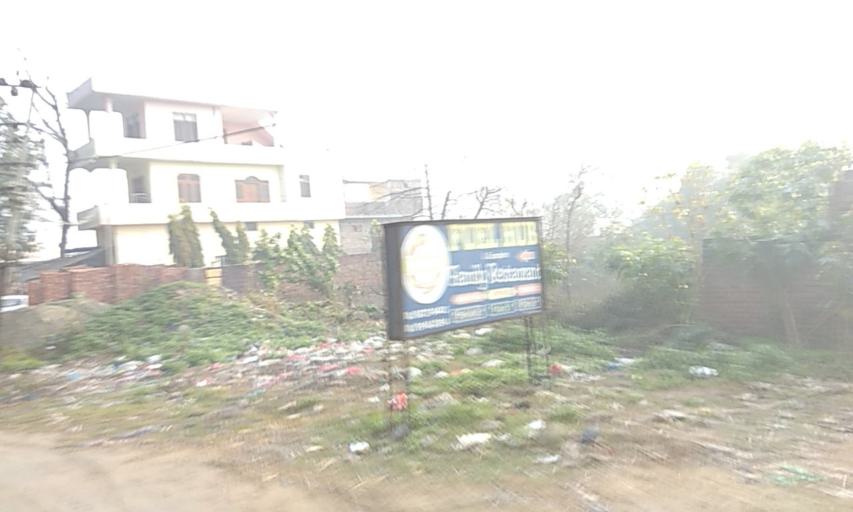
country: IN
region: Punjab
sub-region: Gurdaspur
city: Dhariwal
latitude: 31.9450
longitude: 75.3143
